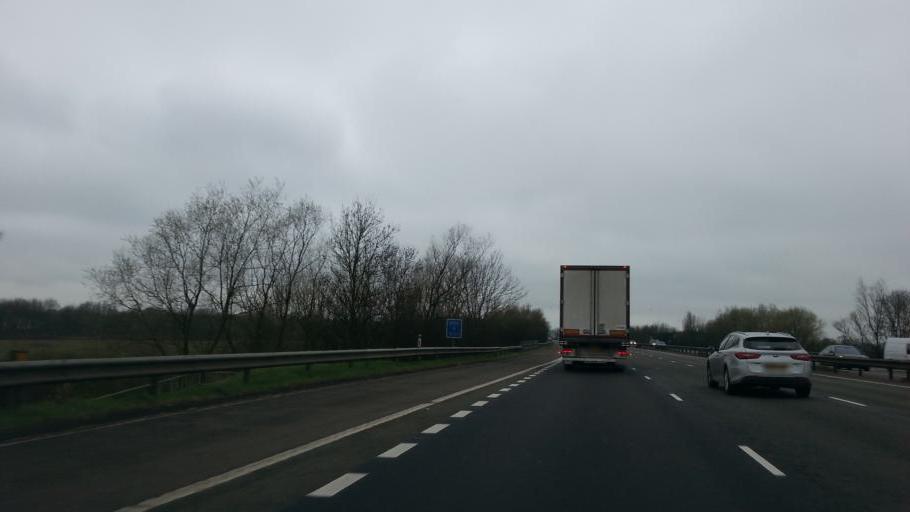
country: GB
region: England
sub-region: Oxfordshire
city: Banbury
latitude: 52.0811
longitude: -1.3212
